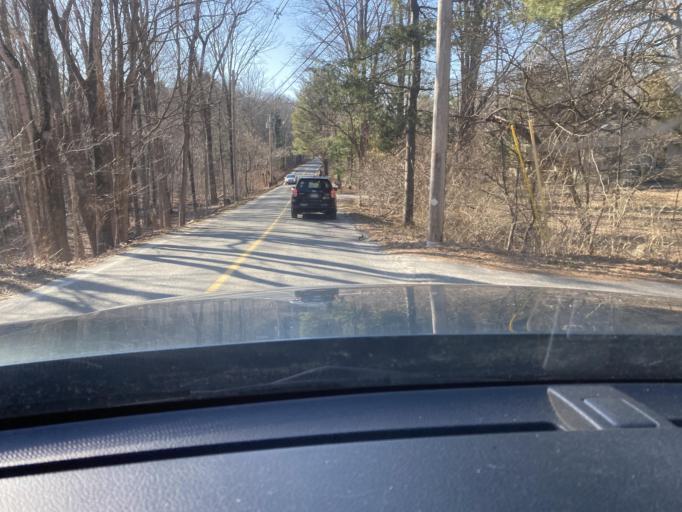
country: US
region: Massachusetts
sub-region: Middlesex County
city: Sherborn
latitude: 42.2279
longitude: -71.3586
